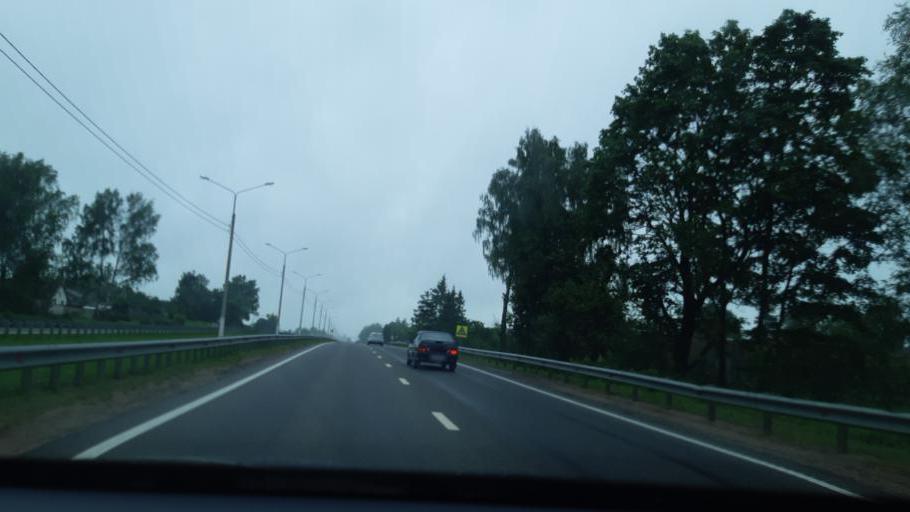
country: RU
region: Smolensk
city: Talashkino
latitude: 54.6719
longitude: 32.1488
